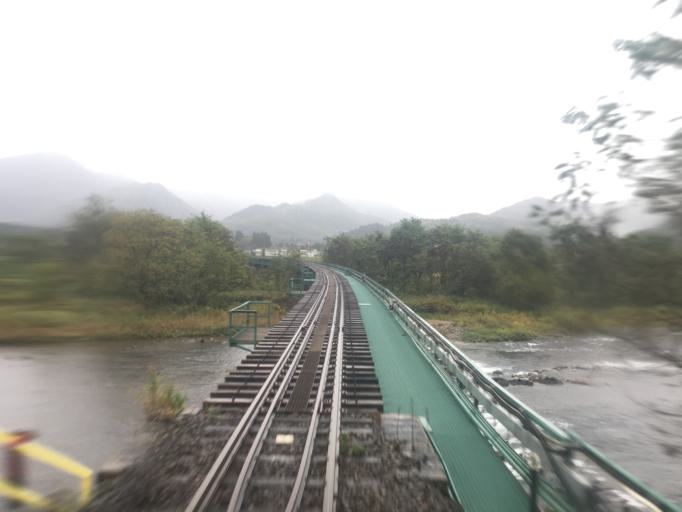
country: JP
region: Yamagata
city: Shinjo
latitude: 38.7154
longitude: 140.3773
